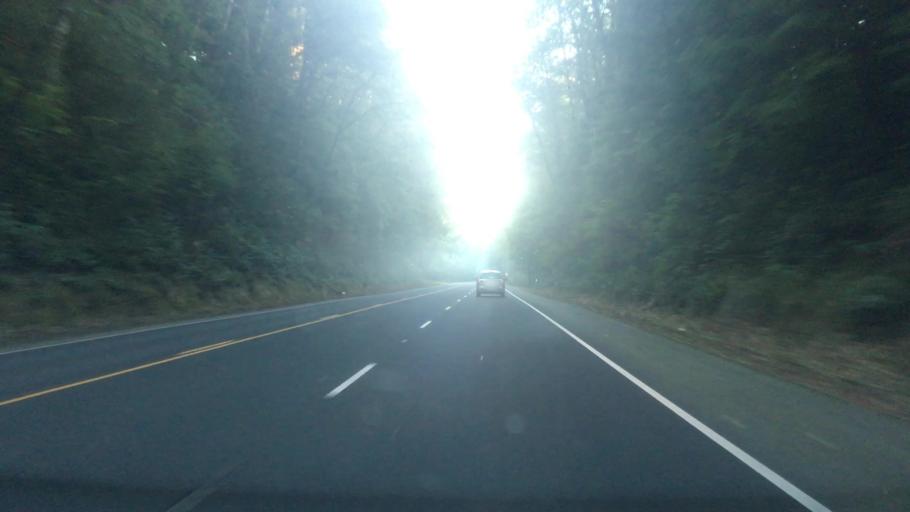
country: US
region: Oregon
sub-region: Clatsop County
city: Cannon Beach
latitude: 45.7907
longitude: -123.9602
